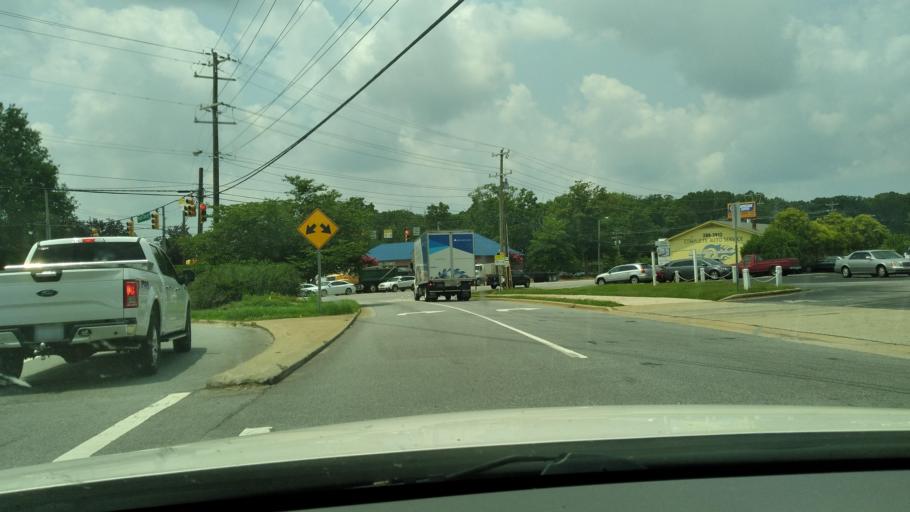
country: US
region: North Carolina
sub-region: Guilford County
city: Greensboro
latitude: 36.1164
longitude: -79.8364
